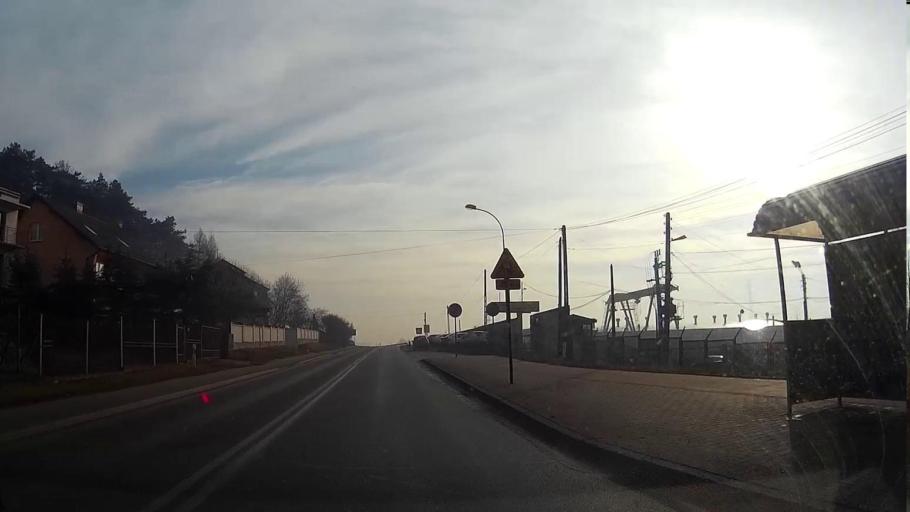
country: PL
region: Lesser Poland Voivodeship
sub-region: Powiat krakowski
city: Kryspinow
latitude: 50.0416
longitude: 19.7987
